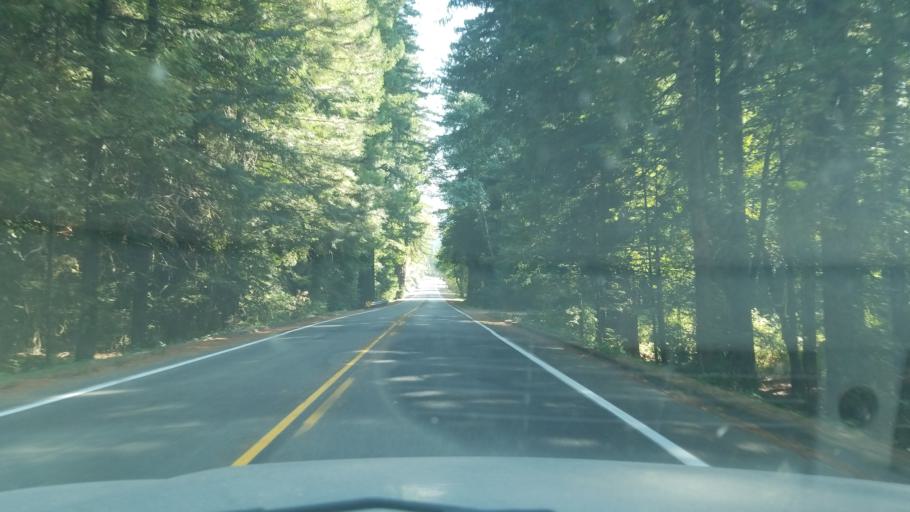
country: US
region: California
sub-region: Humboldt County
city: Redway
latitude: 40.2187
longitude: -123.7861
